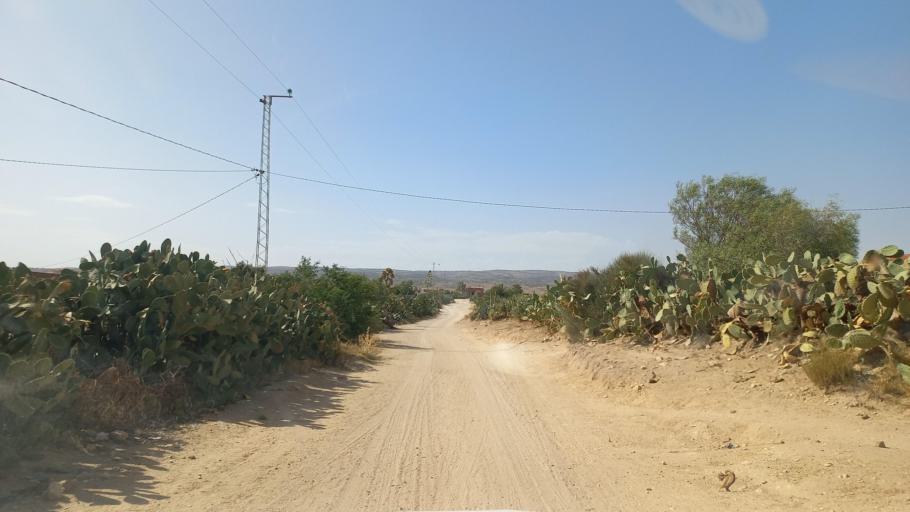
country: TN
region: Al Qasrayn
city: Kasserine
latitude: 35.2737
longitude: 8.9470
